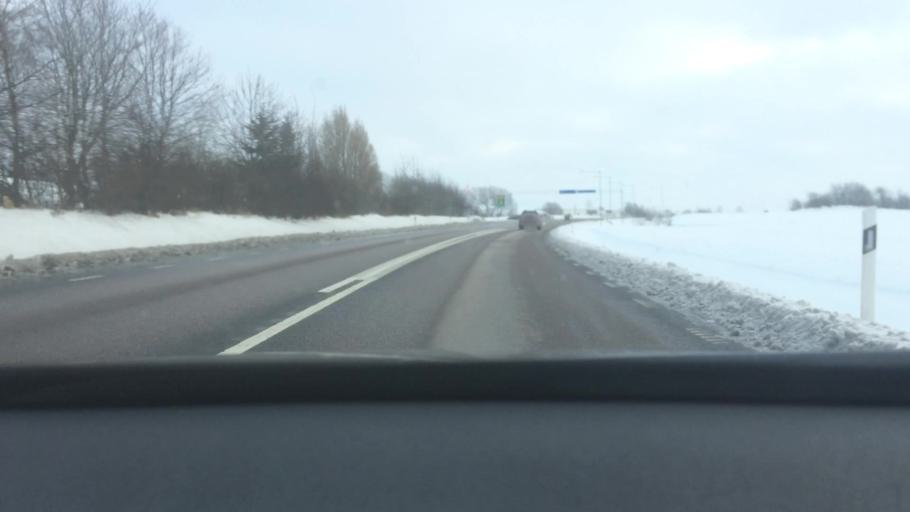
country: SE
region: Vaestra Goetaland
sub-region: Falkopings Kommun
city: Falkoeping
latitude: 58.2279
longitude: 13.5604
